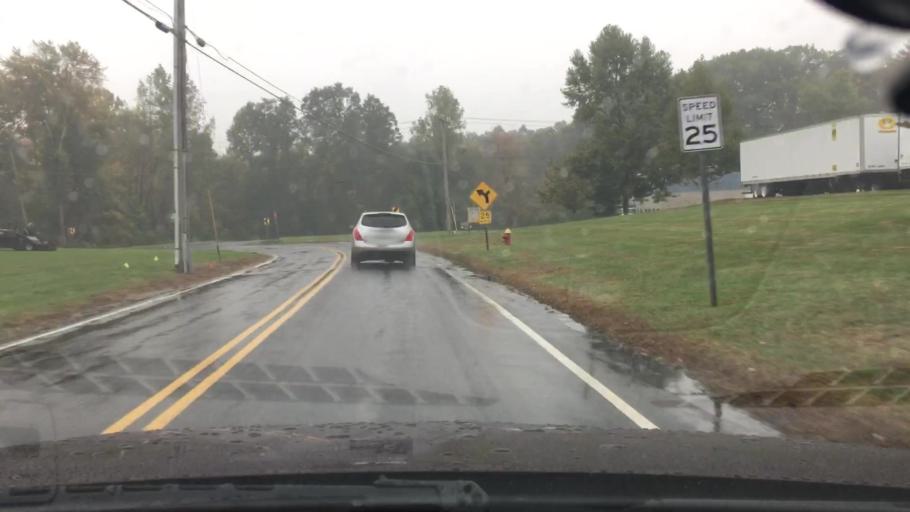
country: US
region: Connecticut
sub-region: Hartford County
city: Blue Hills
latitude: 41.8556
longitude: -72.7193
